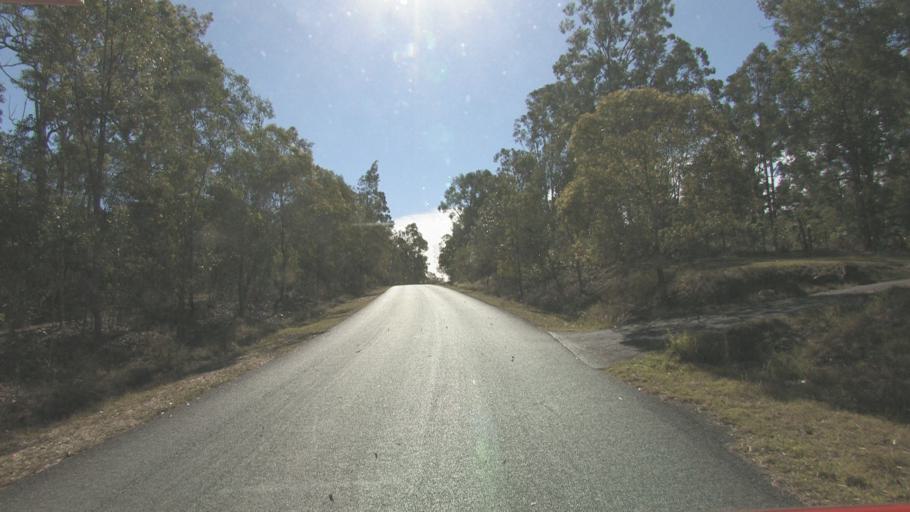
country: AU
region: Queensland
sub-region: Ipswich
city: Springfield Lakes
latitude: -27.7134
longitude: 152.9319
